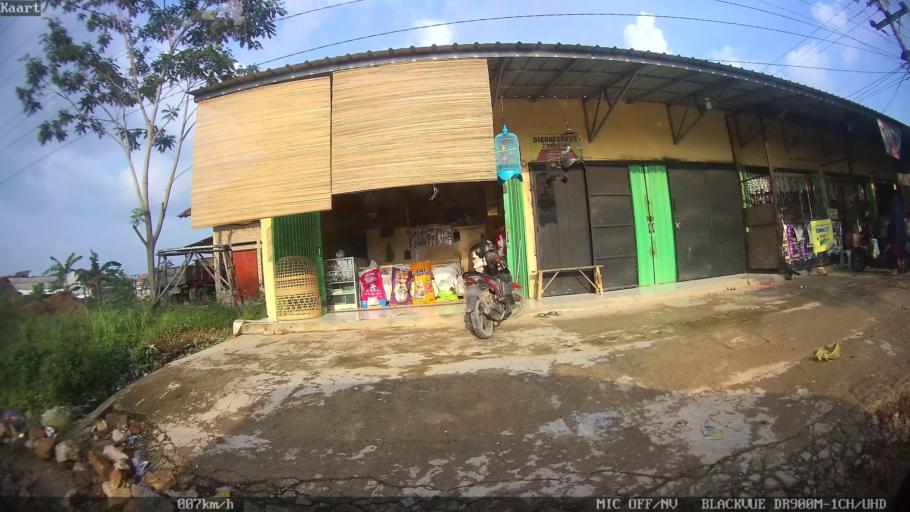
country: ID
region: Lampung
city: Kedaton
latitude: -5.3916
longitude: 105.3237
